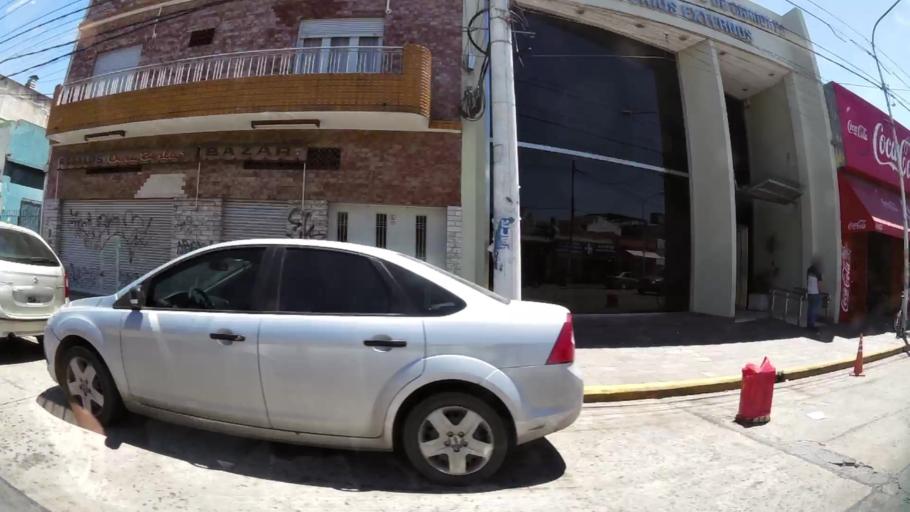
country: AR
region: Buenos Aires
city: Caseros
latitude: -34.5957
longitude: -58.5615
